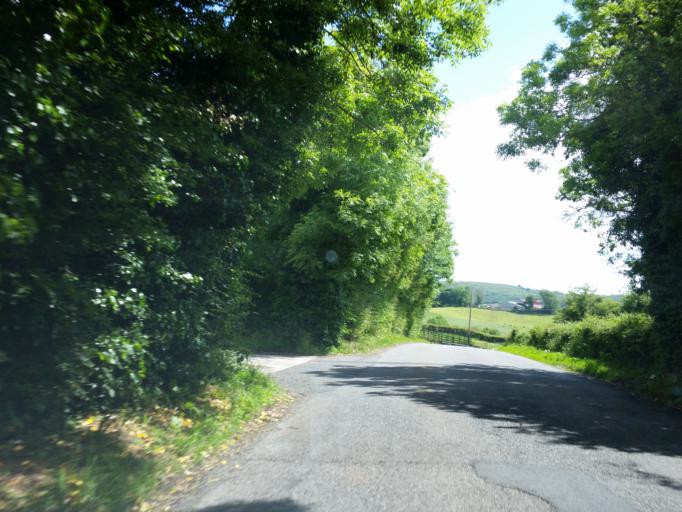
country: GB
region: Northern Ireland
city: Fivemiletown
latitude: 54.3748
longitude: -7.3141
